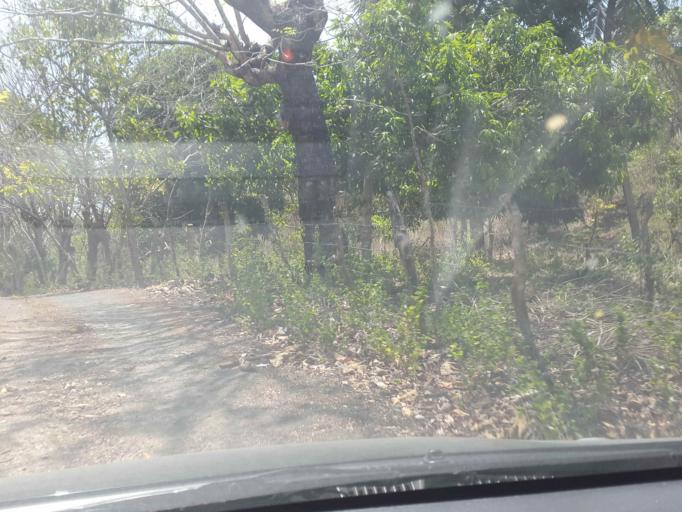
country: ID
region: South Sulawesi
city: Bantaeng
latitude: -6.1676
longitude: 120.4486
